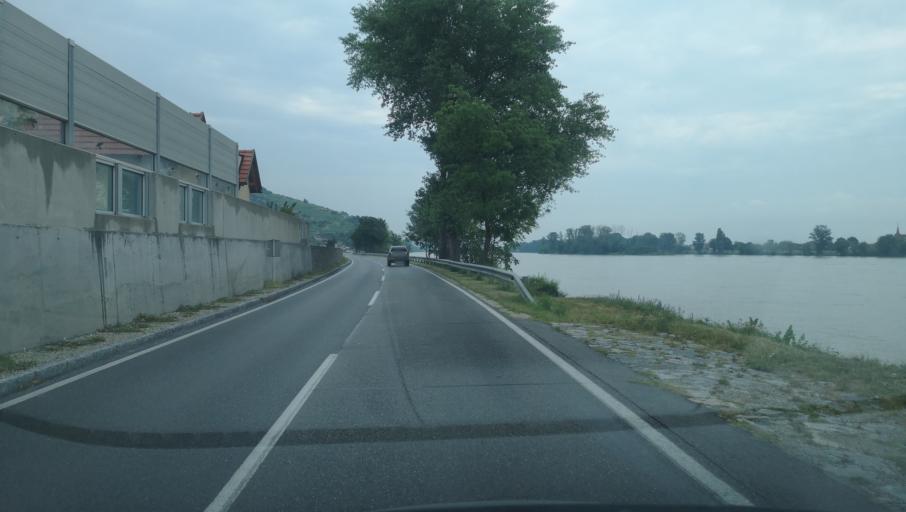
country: AT
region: Lower Austria
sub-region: Politischer Bezirk Krems
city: Durnstein
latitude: 48.3877
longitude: 15.5463
